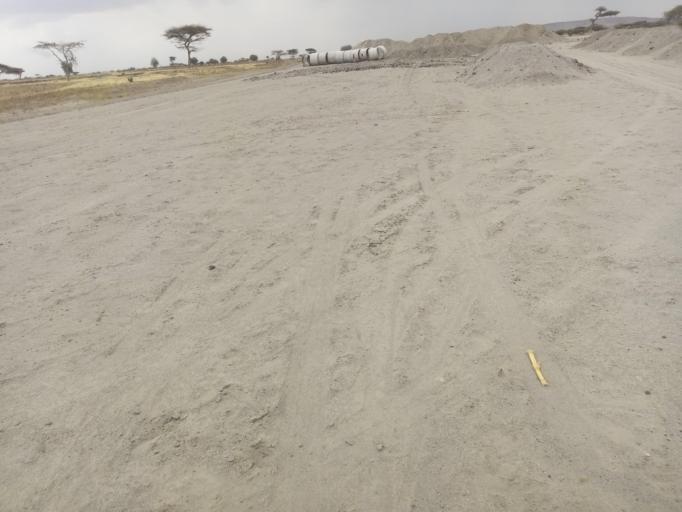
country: ET
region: Oromiya
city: Ziway
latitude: 7.8492
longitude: 38.6622
